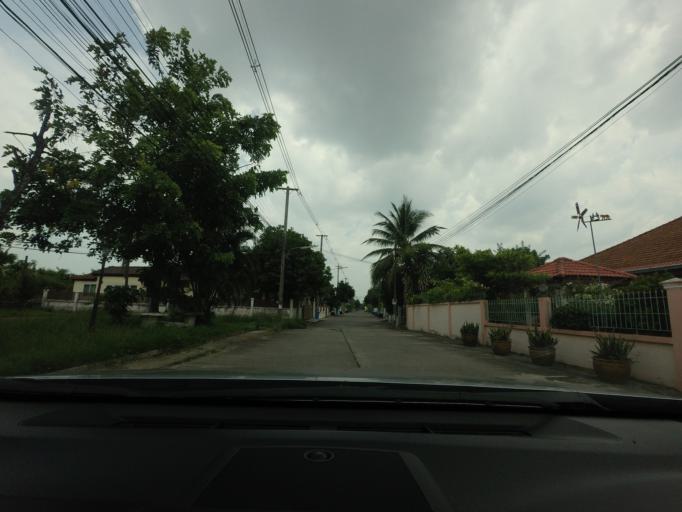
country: TH
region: Nakhon Si Thammarat
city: Nakhon Si Thammarat
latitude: 8.4490
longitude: 99.9966
